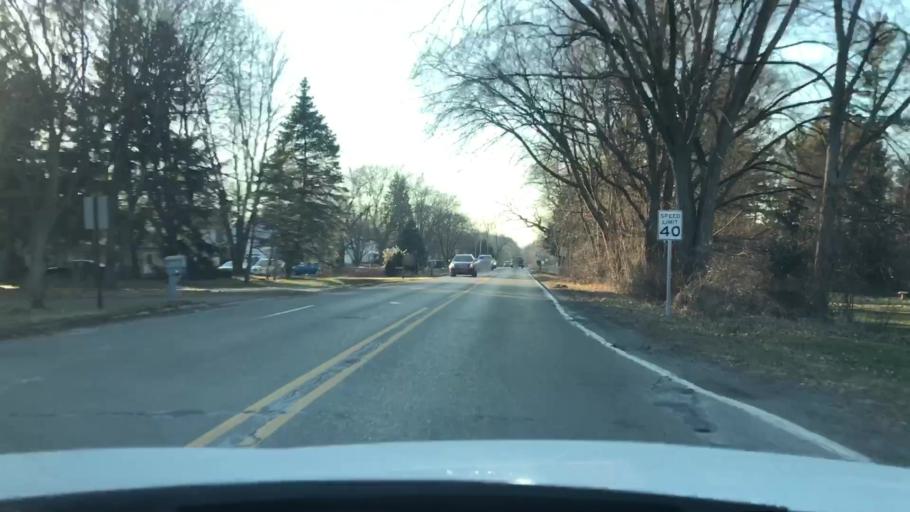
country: US
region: Michigan
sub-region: Oakland County
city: West Bloomfield Township
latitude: 42.5997
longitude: -83.4130
